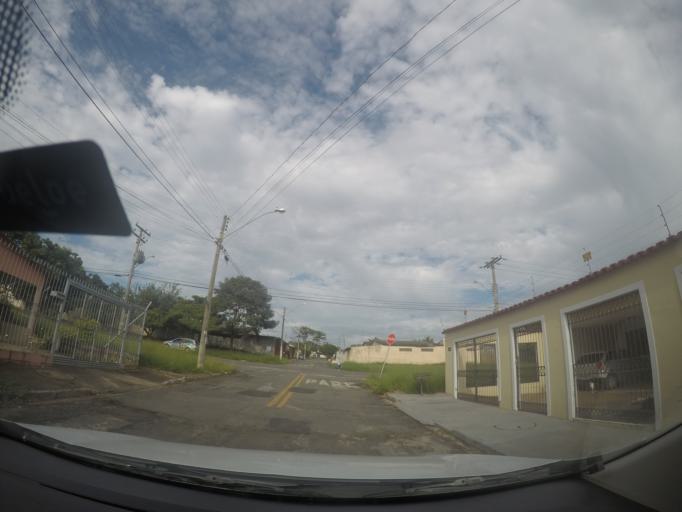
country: BR
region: Goias
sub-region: Goiania
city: Goiania
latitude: -16.6819
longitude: -49.2017
